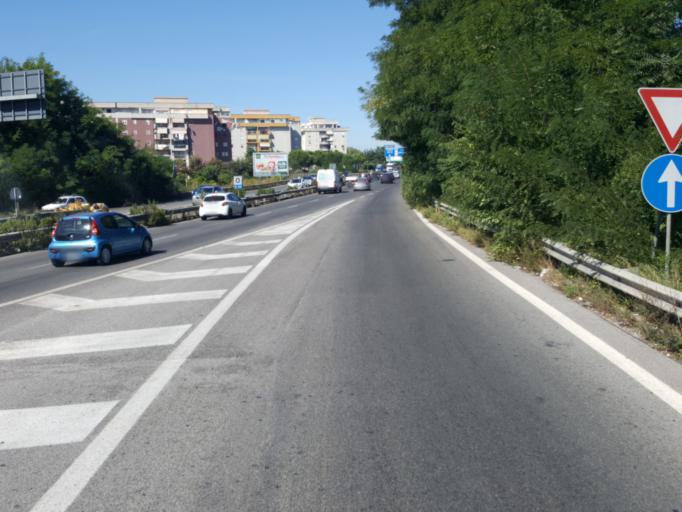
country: IT
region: Campania
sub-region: Provincia di Napoli
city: Casandrino
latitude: 40.9274
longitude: 14.2383
